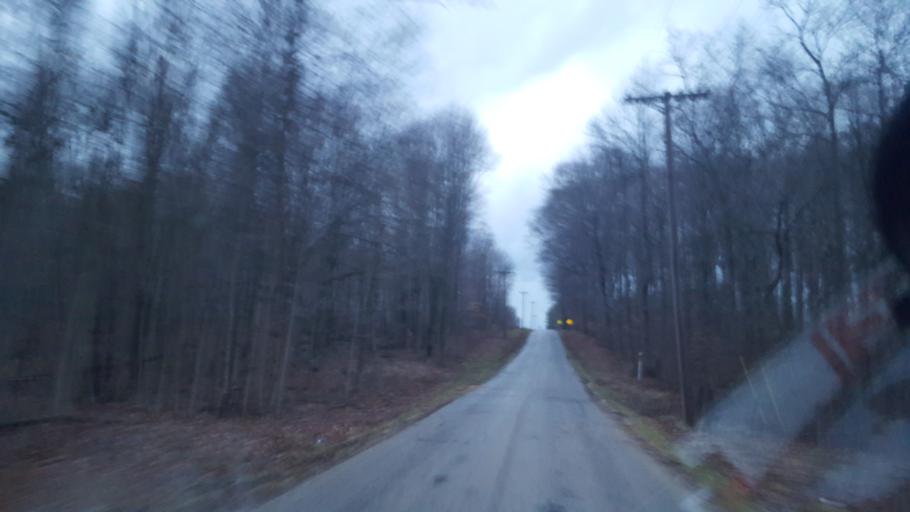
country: US
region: Ohio
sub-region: Richland County
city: Lexington
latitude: 40.5918
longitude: -82.6052
